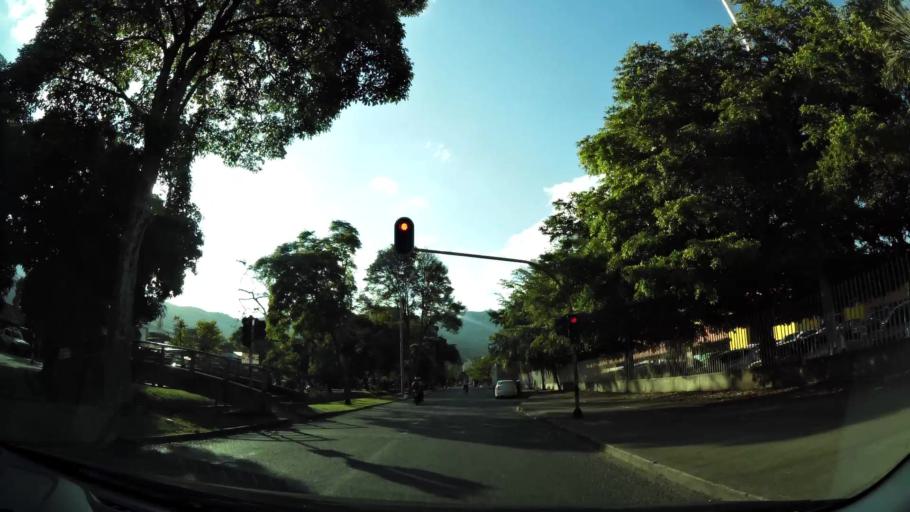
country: CO
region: Valle del Cauca
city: Cali
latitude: 3.4860
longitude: -76.5170
